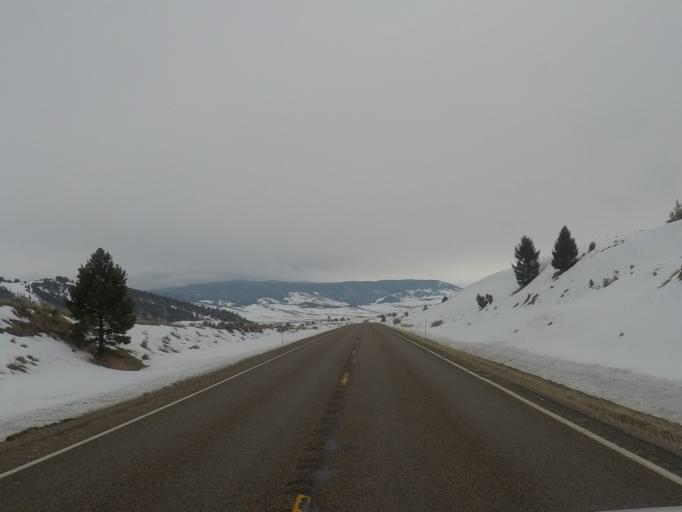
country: US
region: Montana
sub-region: Meagher County
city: White Sulphur Springs
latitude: 46.6207
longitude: -110.8462
